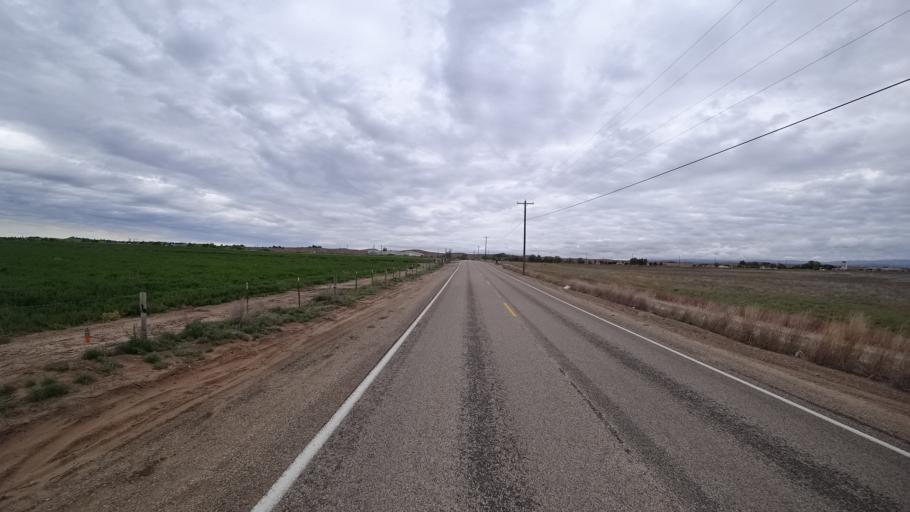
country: US
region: Idaho
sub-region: Ada County
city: Star
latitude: 43.7152
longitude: -116.4434
